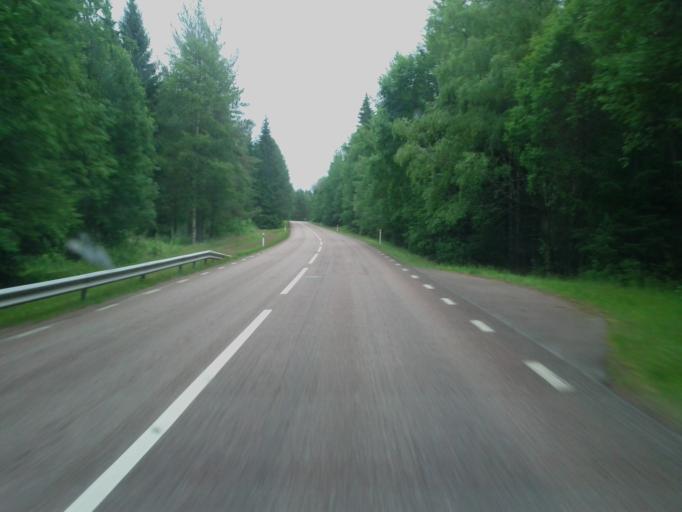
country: SE
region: Dalarna
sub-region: Mora Kommun
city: Mora
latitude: 61.0874
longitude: 14.3149
